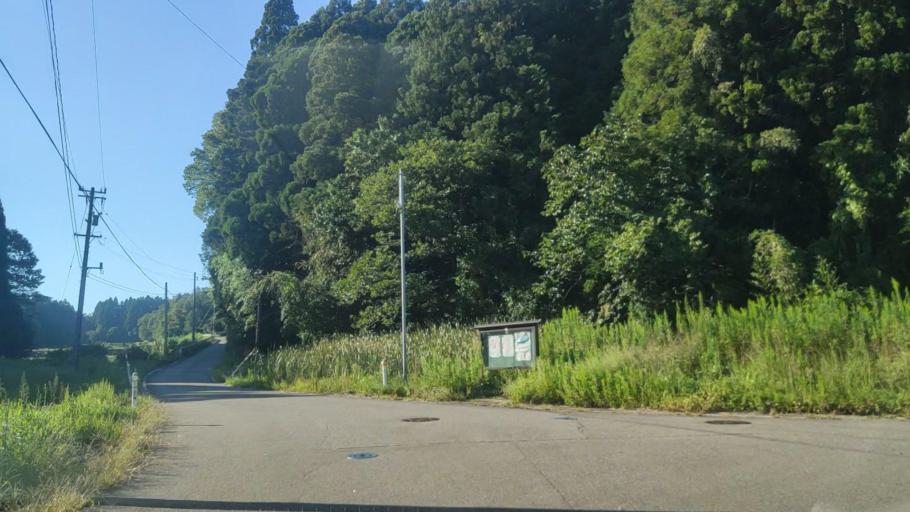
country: JP
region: Ishikawa
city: Nanao
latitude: 37.1284
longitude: 136.8955
